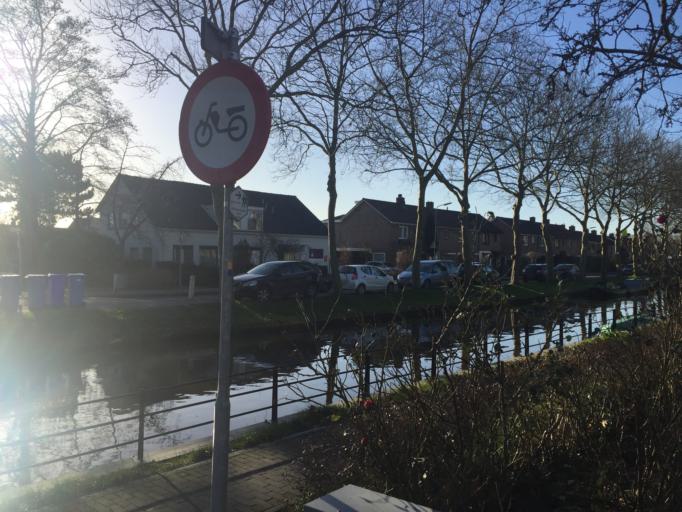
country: NL
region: Utrecht
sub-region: Gemeente Montfoort
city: Montfoort
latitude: 52.0905
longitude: 4.9610
